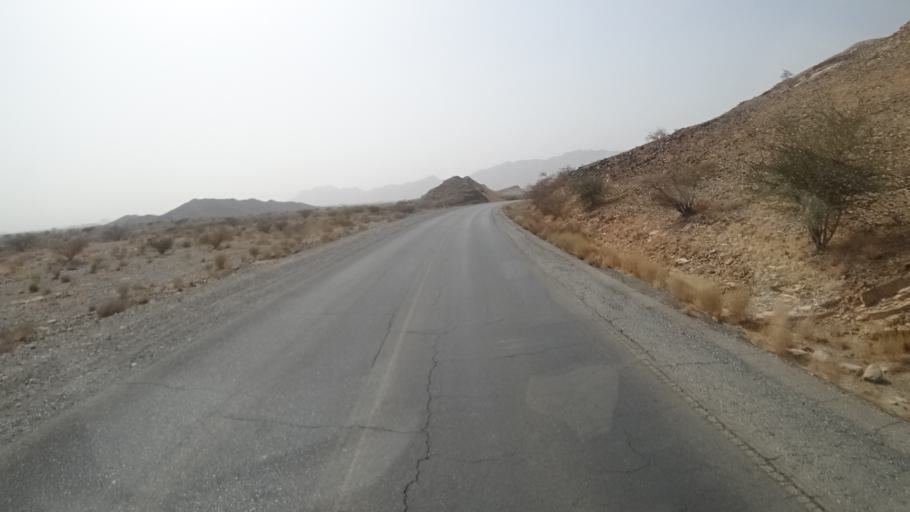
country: OM
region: Muhafazat ad Dakhiliyah
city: Nizwa
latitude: 22.9244
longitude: 57.6475
